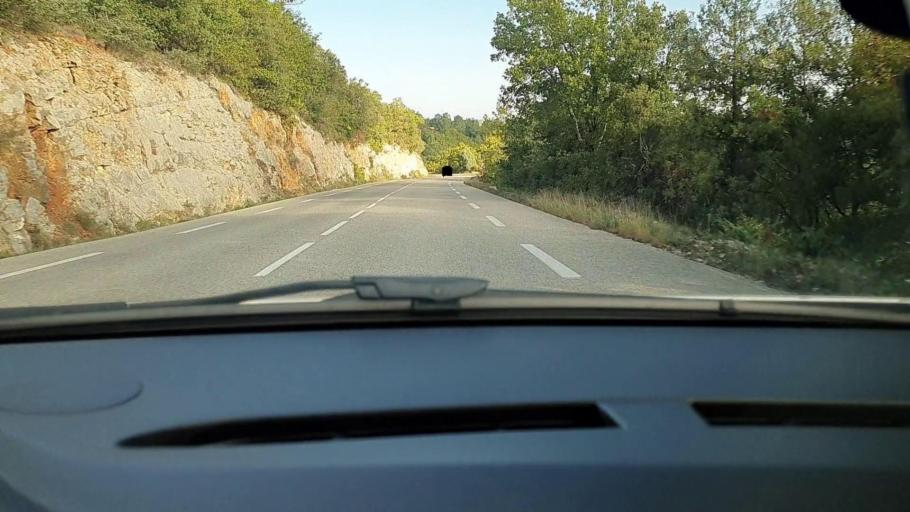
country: FR
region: Languedoc-Roussillon
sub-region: Departement du Gard
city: Barjac
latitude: 44.2334
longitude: 4.3056
